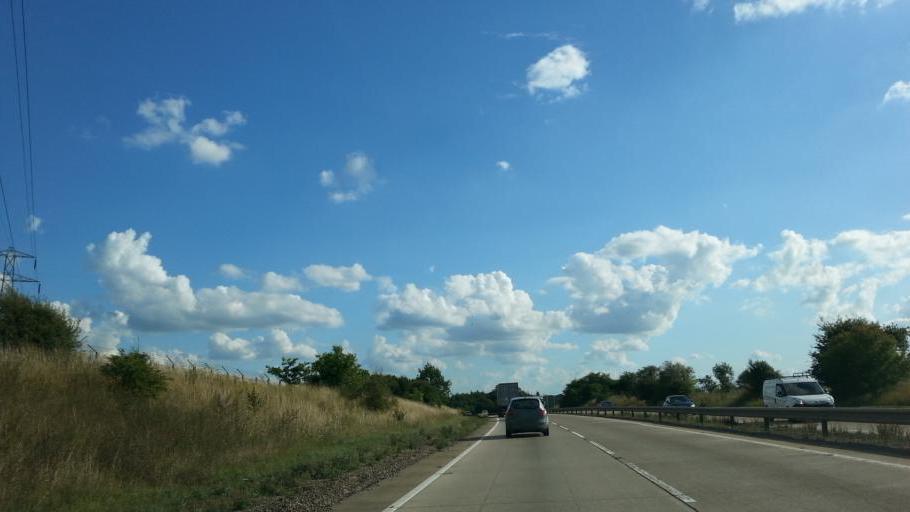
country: GB
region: England
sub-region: Suffolk
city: Bramford
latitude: 52.0445
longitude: 1.0955
